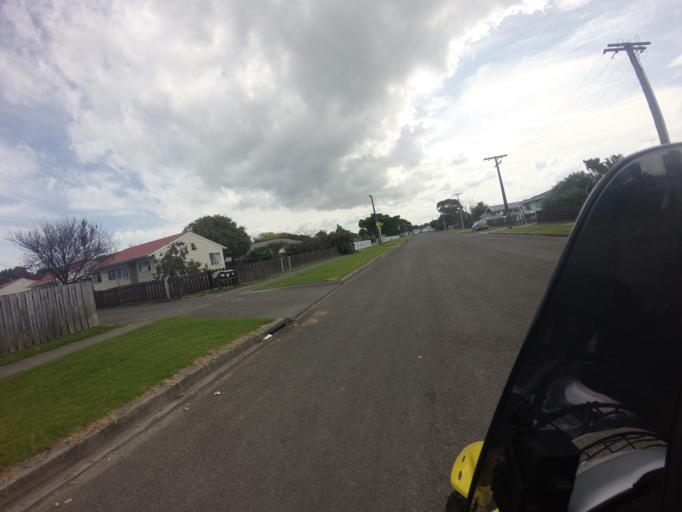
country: NZ
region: Gisborne
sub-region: Gisborne District
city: Gisborne
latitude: -38.6767
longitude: 178.0502
